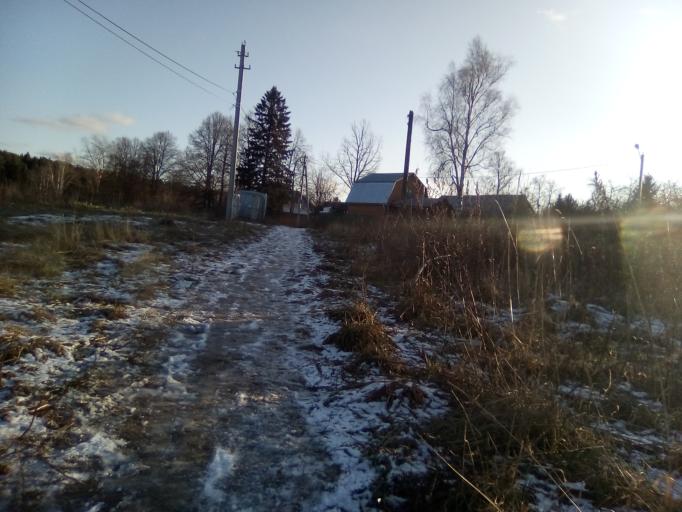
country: RU
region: Moskovskaya
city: Lesnoy Gorodok
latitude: 55.6495
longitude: 37.1702
